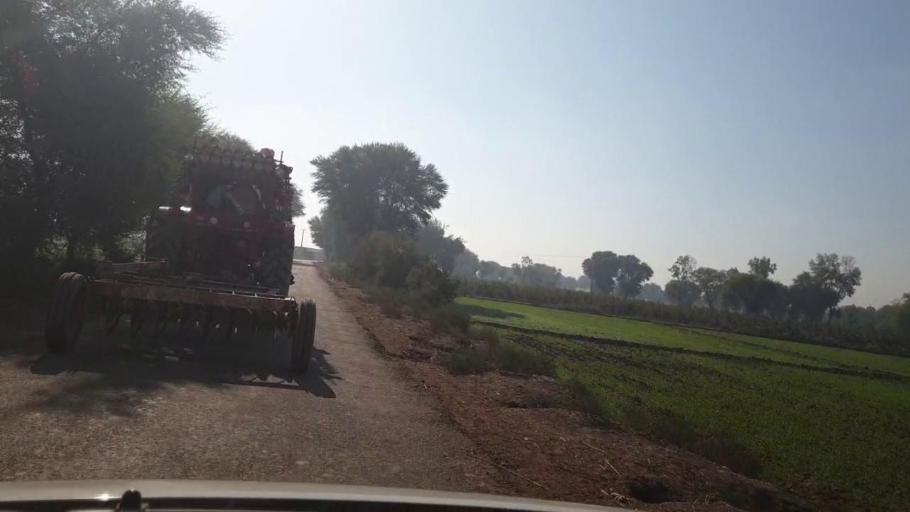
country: PK
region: Sindh
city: Dadu
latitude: 26.6571
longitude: 67.8217
